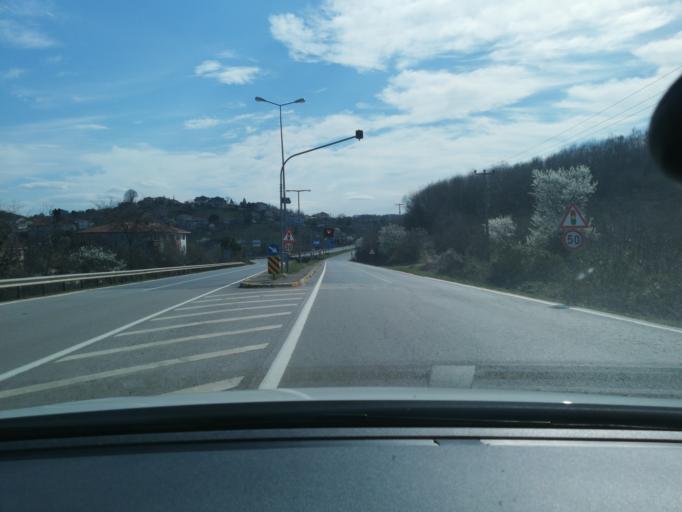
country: TR
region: Duzce
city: Akcakoca
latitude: 41.0869
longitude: 31.1513
